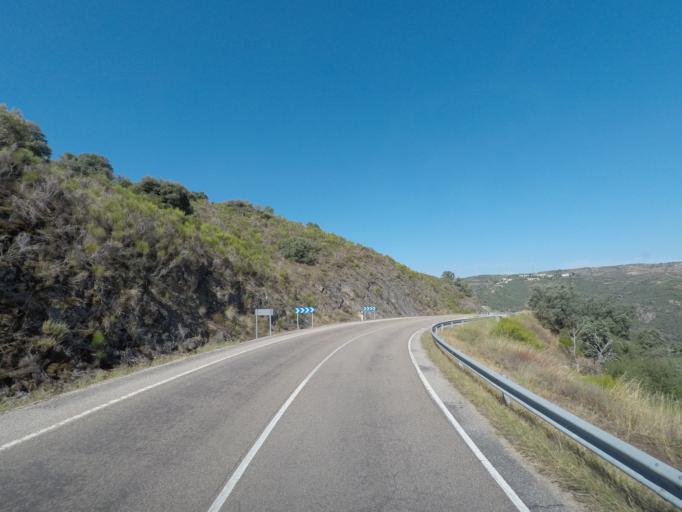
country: ES
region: Castille and Leon
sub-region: Provincia de Salamanca
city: Villarino de los Aires
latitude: 41.2948
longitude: -6.4615
